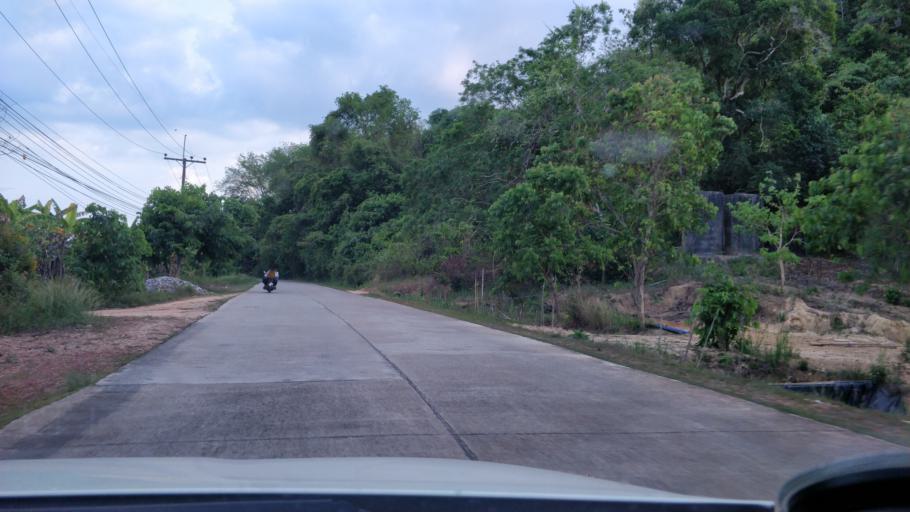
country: TH
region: Krabi
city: Saladan
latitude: 7.5796
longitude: 99.0676
